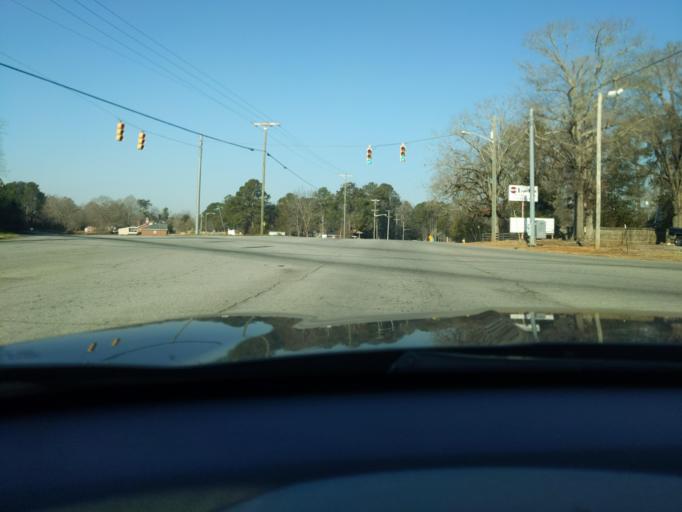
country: US
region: South Carolina
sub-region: Greenwood County
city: Greenwood
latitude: 34.1833
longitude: -82.1085
